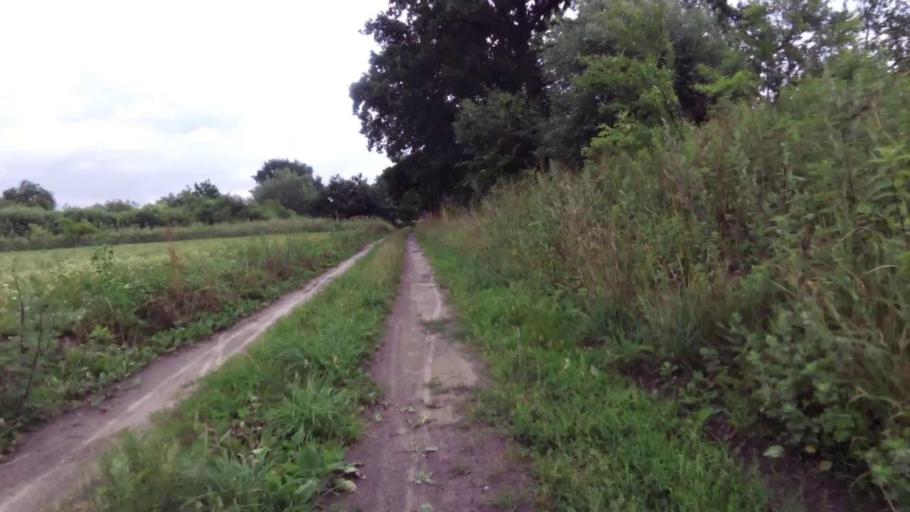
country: PL
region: West Pomeranian Voivodeship
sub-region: Powiat mysliborski
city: Mysliborz
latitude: 52.9633
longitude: 14.9010
